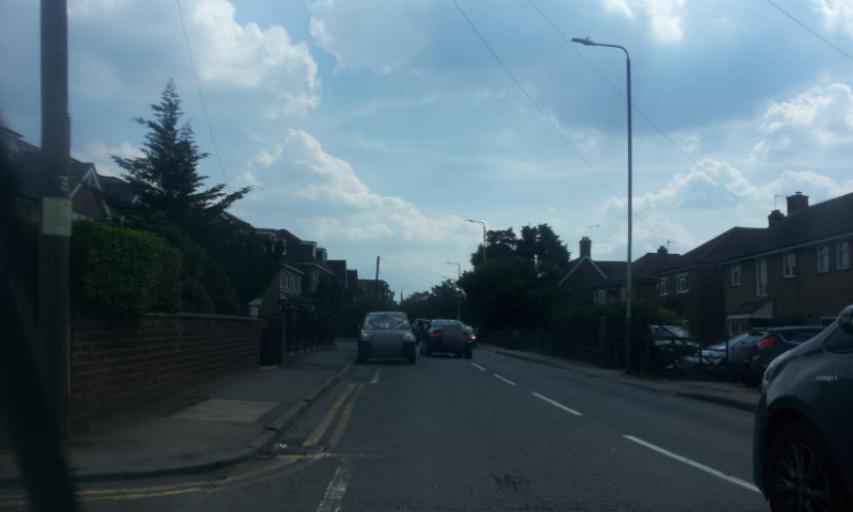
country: GB
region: England
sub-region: Kent
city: Paddock Wood
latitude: 51.1859
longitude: 0.3880
